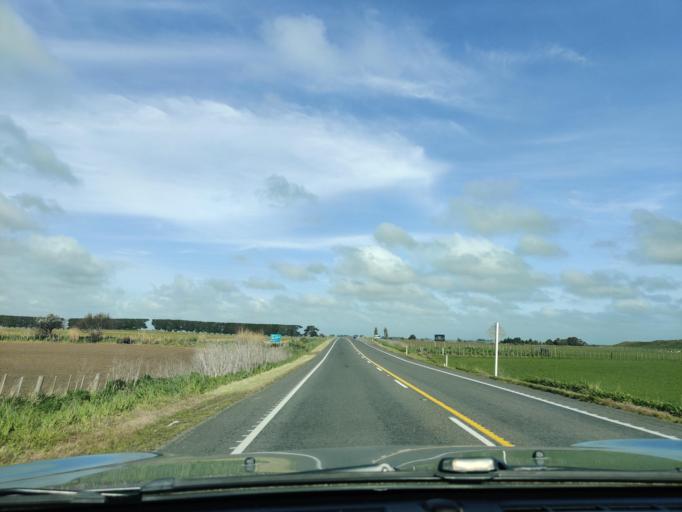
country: NZ
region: Manawatu-Wanganui
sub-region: Wanganui District
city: Wanganui
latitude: -39.9908
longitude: 175.1635
